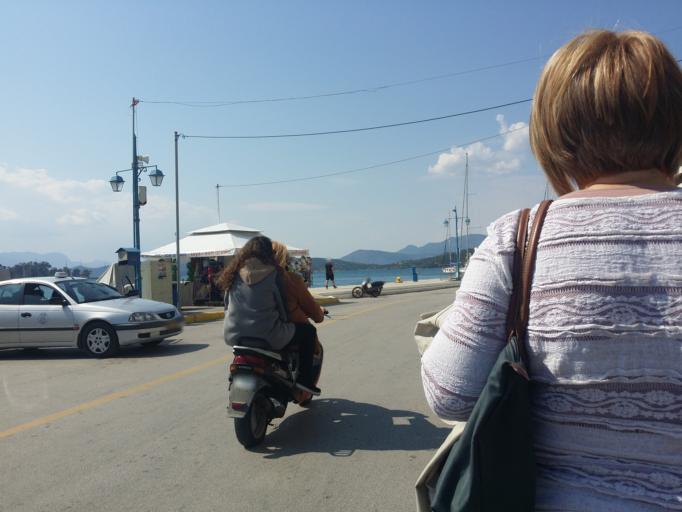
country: GR
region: Attica
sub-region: Nomos Piraios
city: Poros
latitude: 37.4992
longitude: 23.4515
